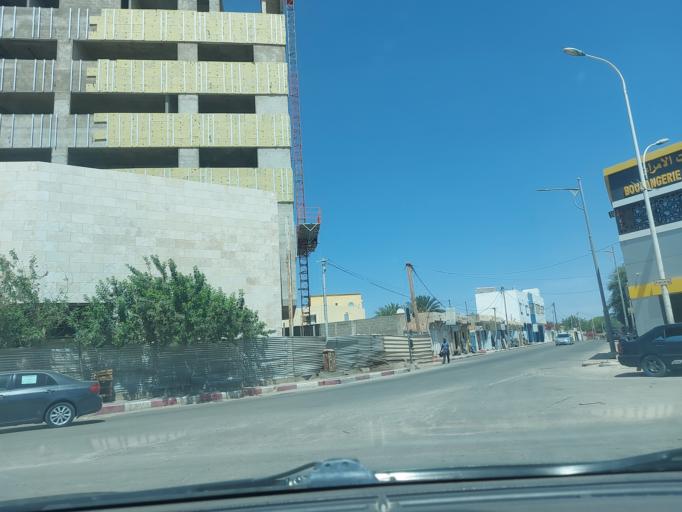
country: MR
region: Nouakchott
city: Nouakchott
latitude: 18.0931
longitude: -15.9793
